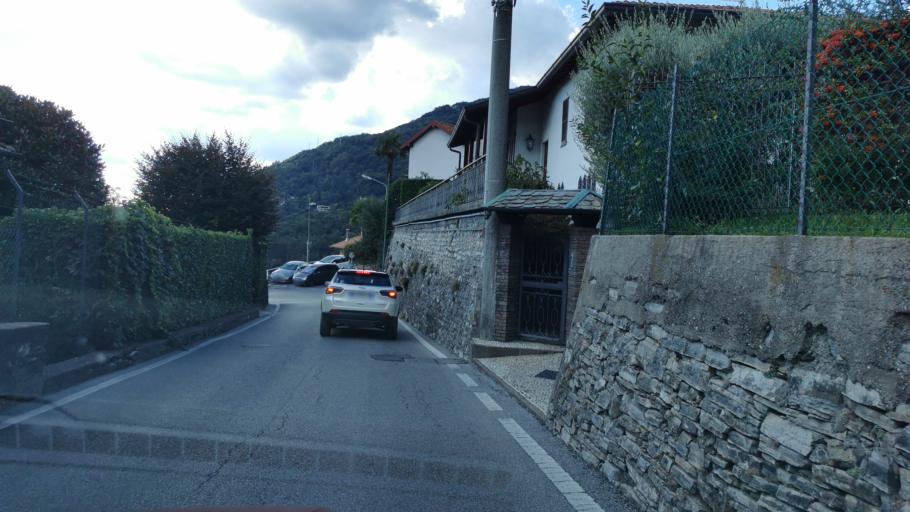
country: IT
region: Lombardy
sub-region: Provincia di Como
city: Cernobbio
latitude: 45.8495
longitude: 9.0799
